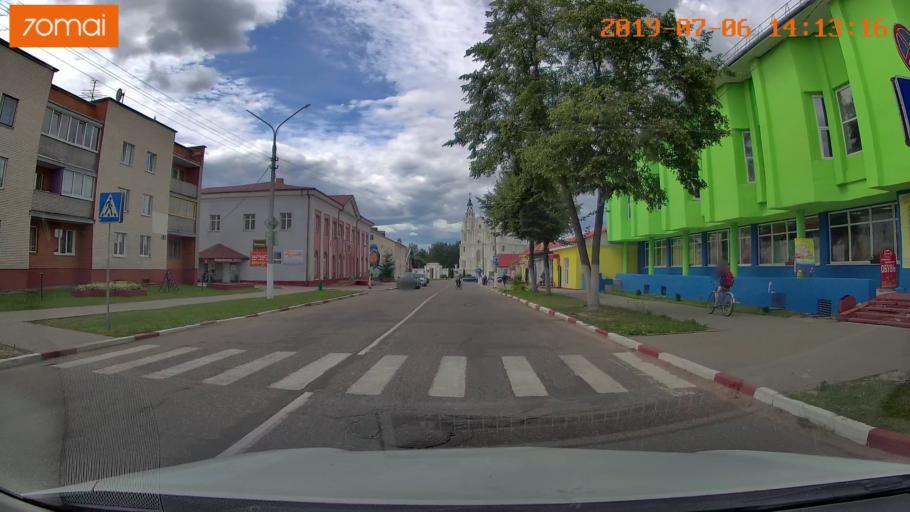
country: BY
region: Minsk
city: Ivyanyets
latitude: 53.8902
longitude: 26.7403
